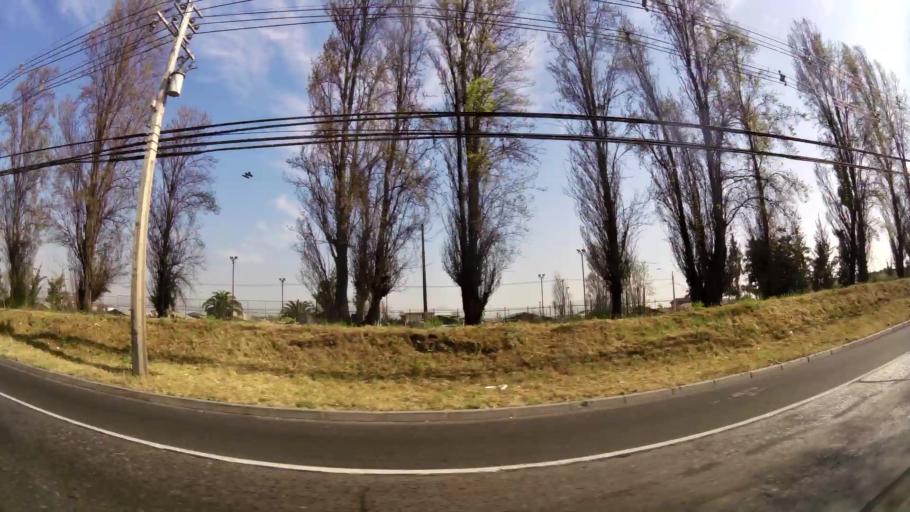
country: CL
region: Santiago Metropolitan
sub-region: Provincia de Maipo
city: San Bernardo
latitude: -33.5343
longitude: -70.7672
